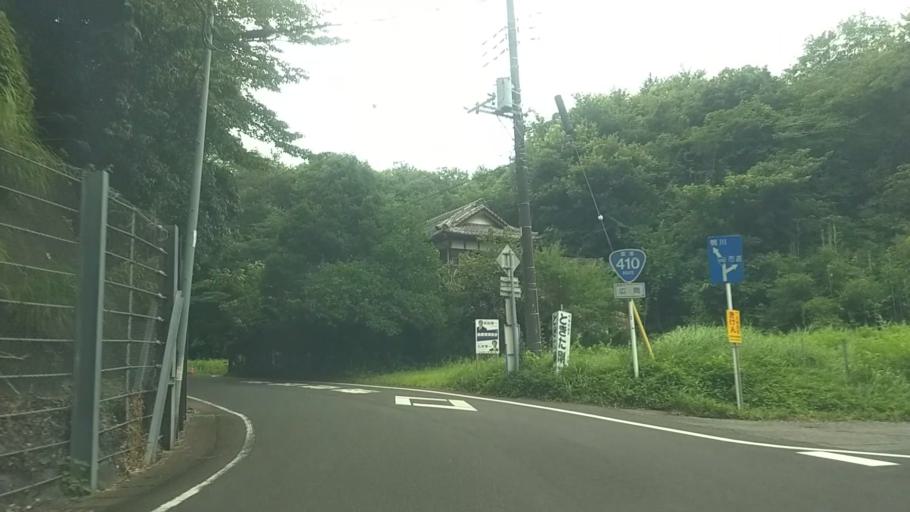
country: JP
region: Chiba
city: Kawaguchi
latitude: 35.2527
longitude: 140.0604
